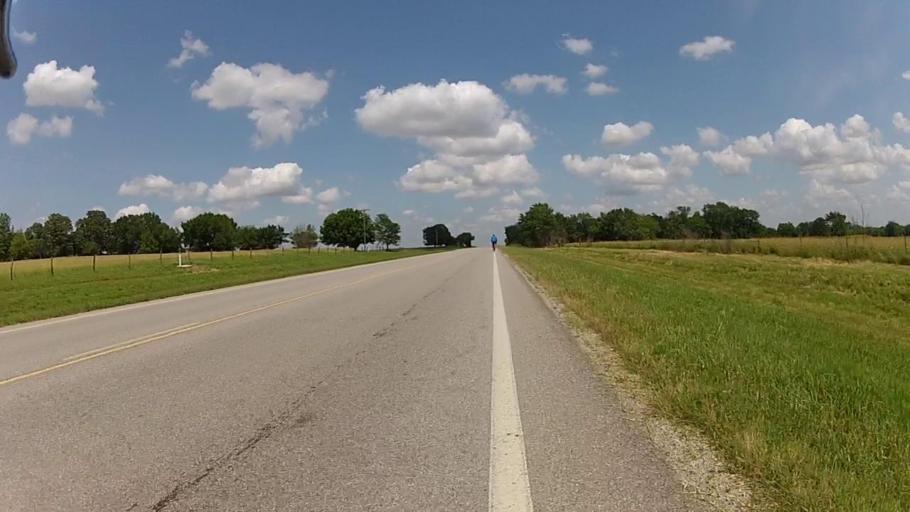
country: US
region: Kansas
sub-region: Labette County
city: Altamont
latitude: 37.1936
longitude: -95.2489
